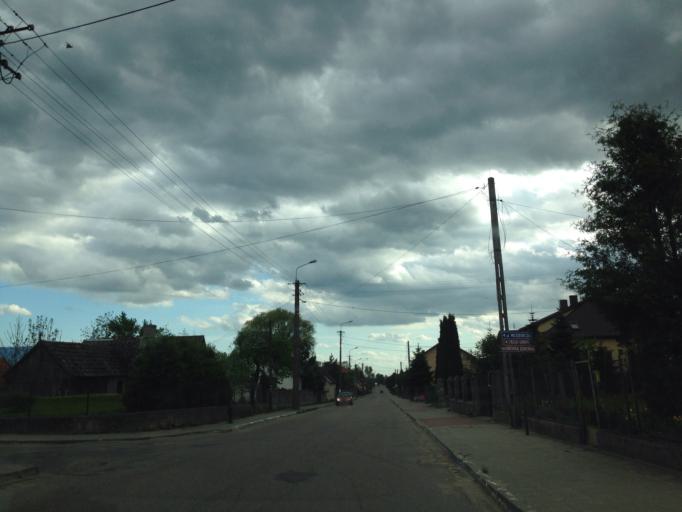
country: PL
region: Podlasie
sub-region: Powiat lomzynski
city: Wizna
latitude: 53.1946
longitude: 22.3822
